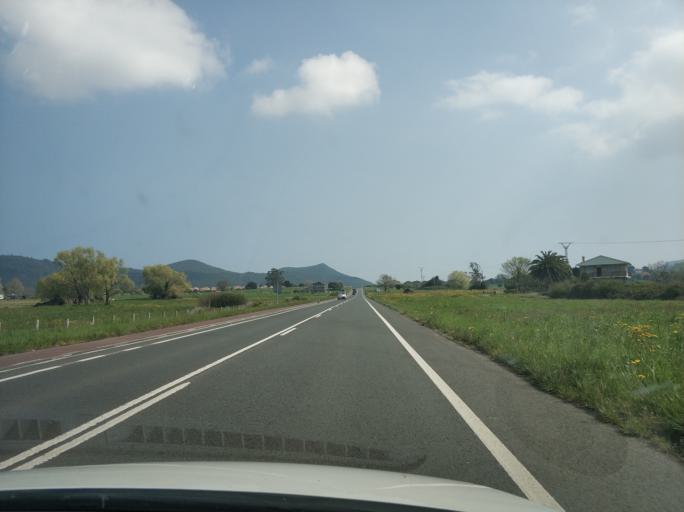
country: ES
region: Cantabria
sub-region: Provincia de Cantabria
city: Escalante
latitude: 43.4421
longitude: -3.5048
